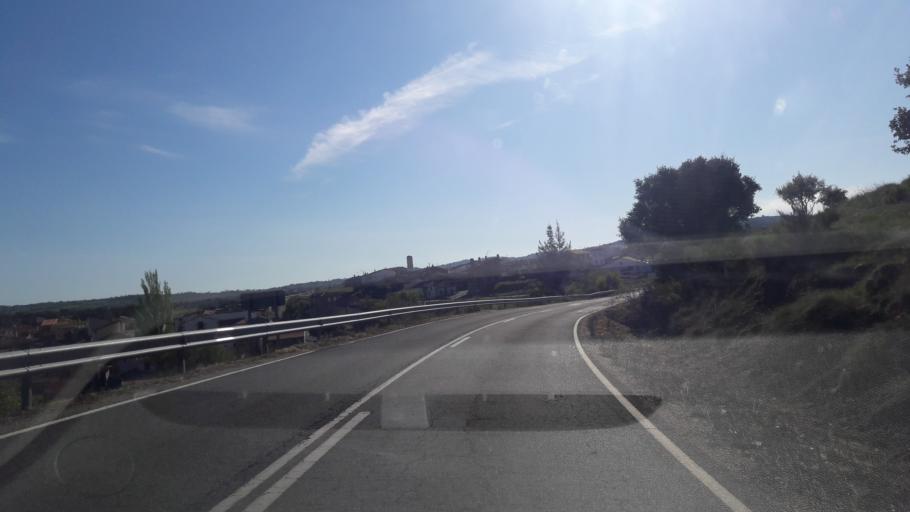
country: ES
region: Castille and Leon
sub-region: Provincia de Avila
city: Narrillos del Alamo
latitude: 40.5345
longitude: -5.4505
